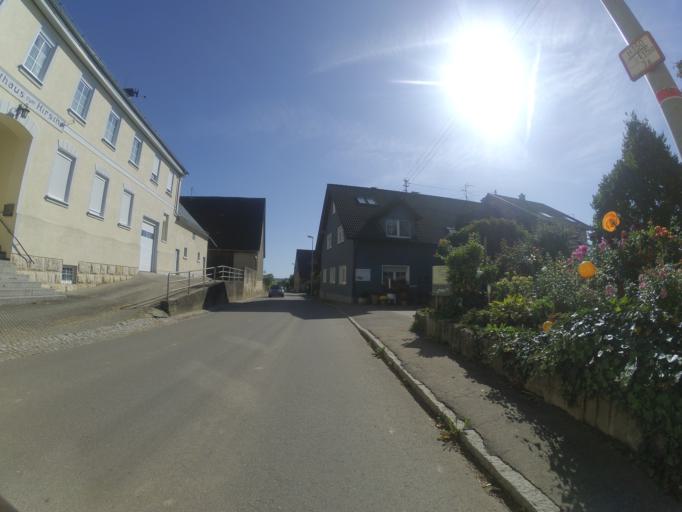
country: DE
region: Baden-Wuerttemberg
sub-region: Tuebingen Region
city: Ballendorf
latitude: 48.5524
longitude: 10.0785
